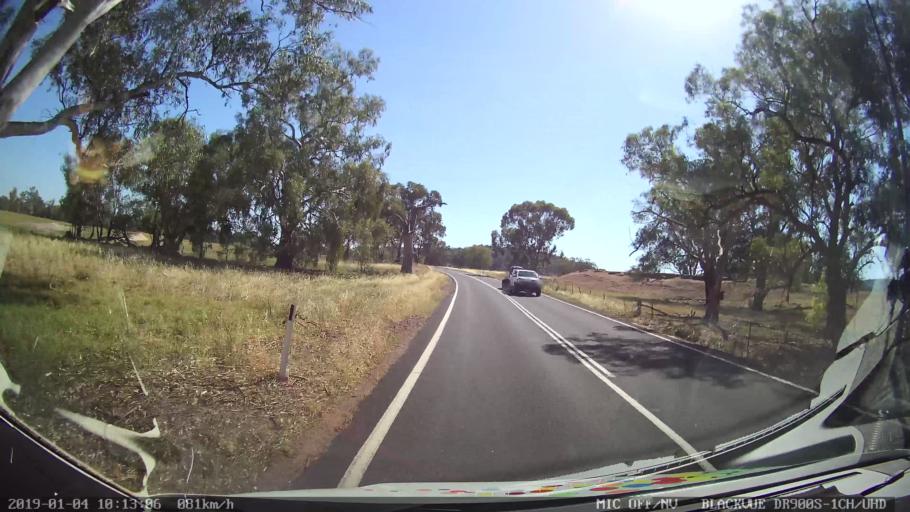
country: AU
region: New South Wales
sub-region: Cabonne
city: Canowindra
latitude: -33.4095
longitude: 148.4032
